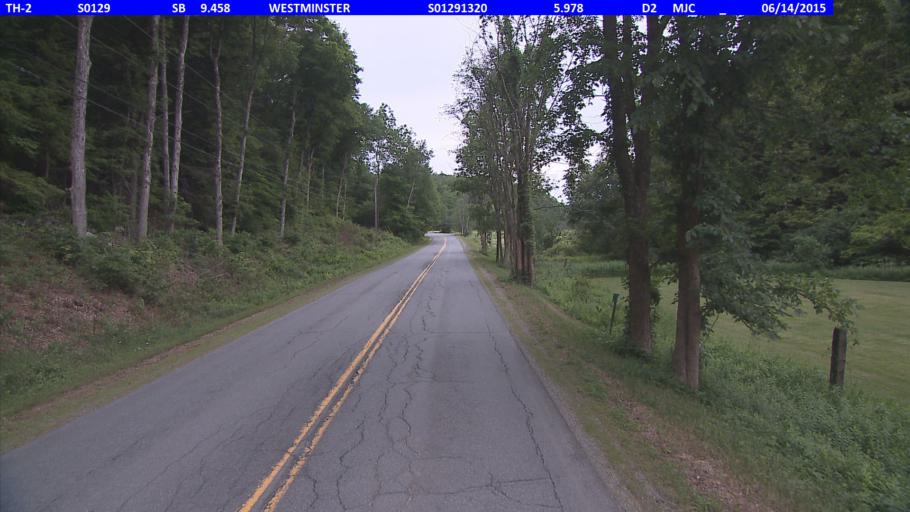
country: US
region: Vermont
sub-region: Windham County
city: Bellows Falls
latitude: 43.1010
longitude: -72.5363
